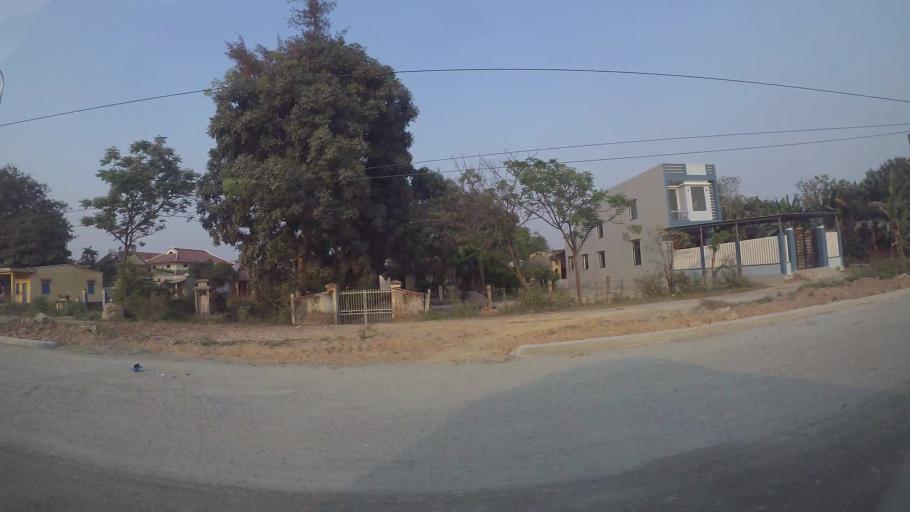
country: VN
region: Da Nang
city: Ngu Hanh Son
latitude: 15.9610
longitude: 108.2317
